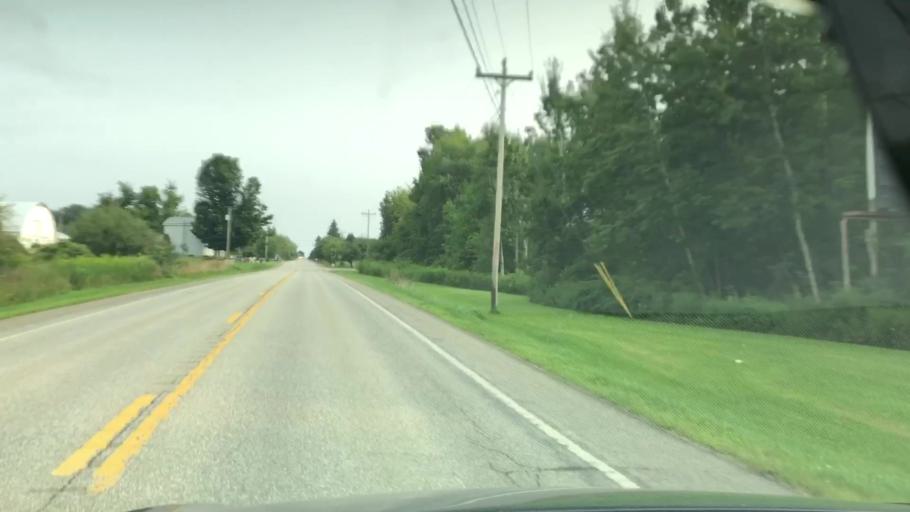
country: US
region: Pennsylvania
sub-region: Erie County
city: Union City
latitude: 41.8820
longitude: -79.8436
